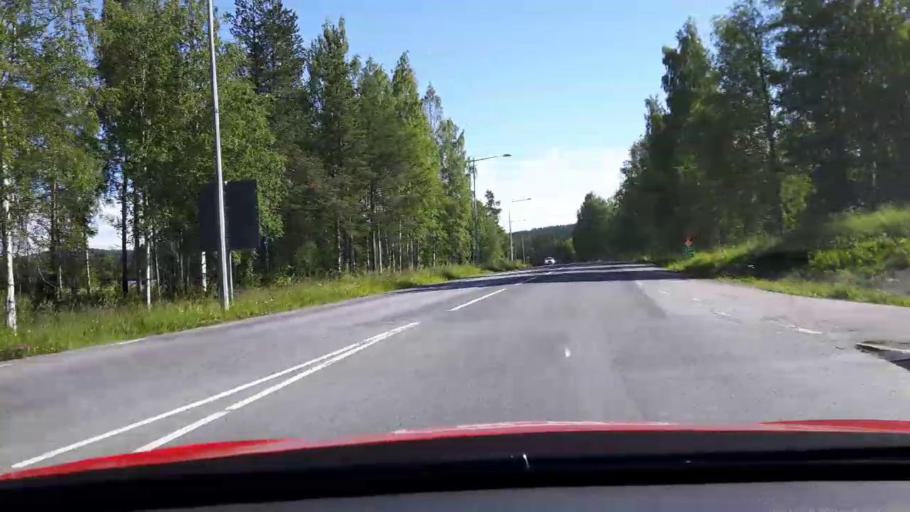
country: SE
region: Jaemtland
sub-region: OEstersunds Kommun
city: Ostersund
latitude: 63.1945
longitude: 14.6632
